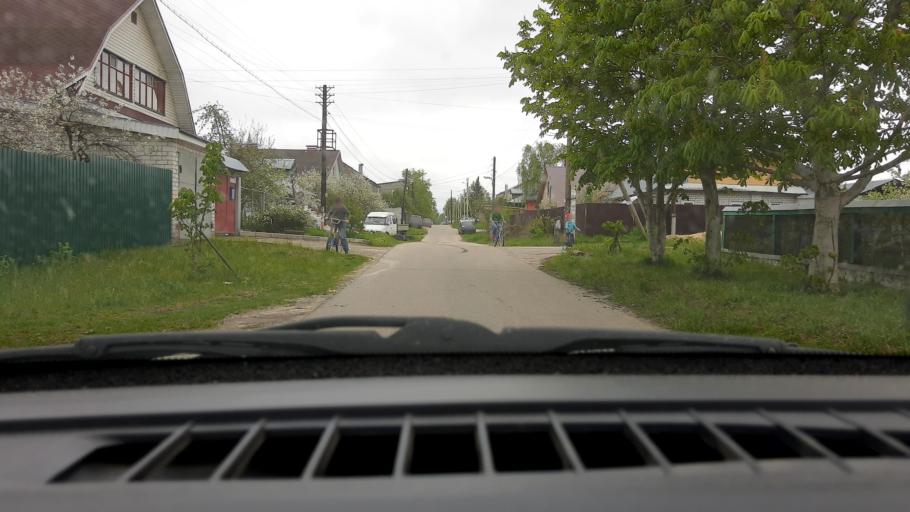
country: RU
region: Nizjnij Novgorod
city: Gorbatovka
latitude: 56.3372
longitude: 43.8258
